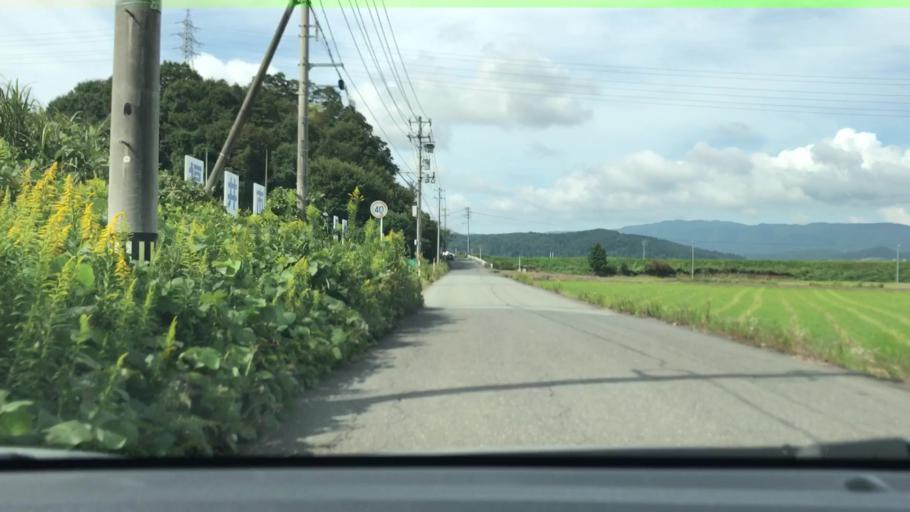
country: JP
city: Asahi
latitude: 36.0140
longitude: 136.1693
